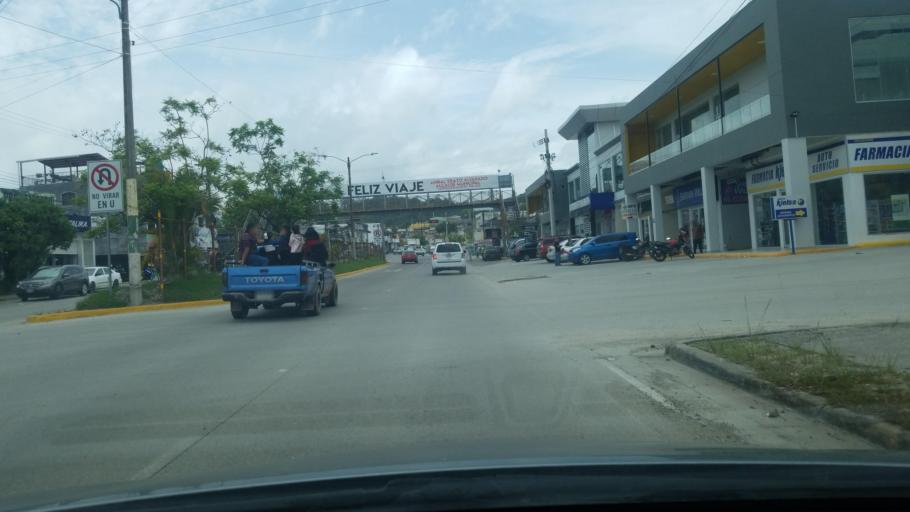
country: HN
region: Copan
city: Santa Rosa de Copan
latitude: 14.7747
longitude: -88.7764
